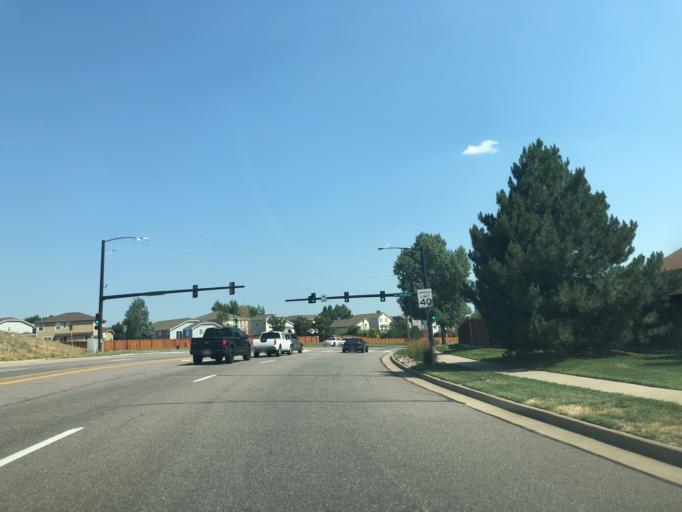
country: US
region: Colorado
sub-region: Arapahoe County
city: Dove Valley
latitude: 39.6314
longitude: -104.7552
